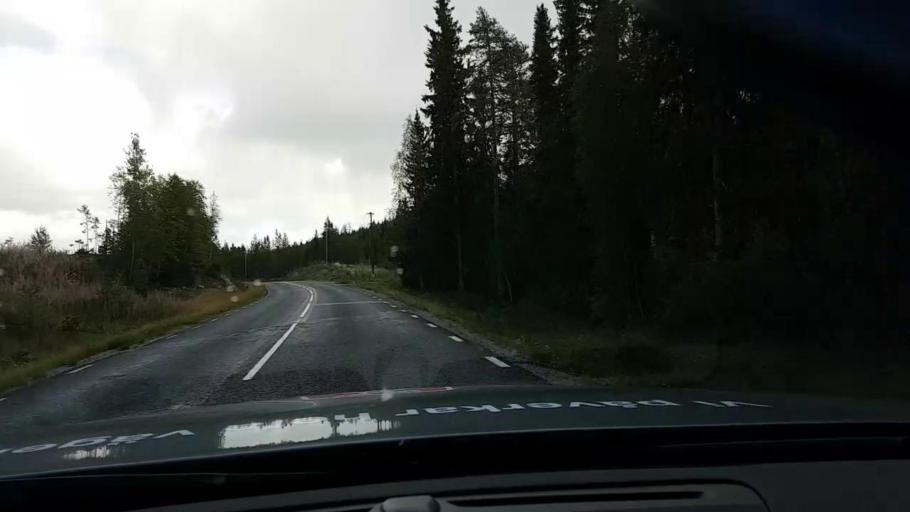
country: SE
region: Vaesterbotten
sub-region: Asele Kommun
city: Asele
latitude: 63.8311
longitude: 17.4532
